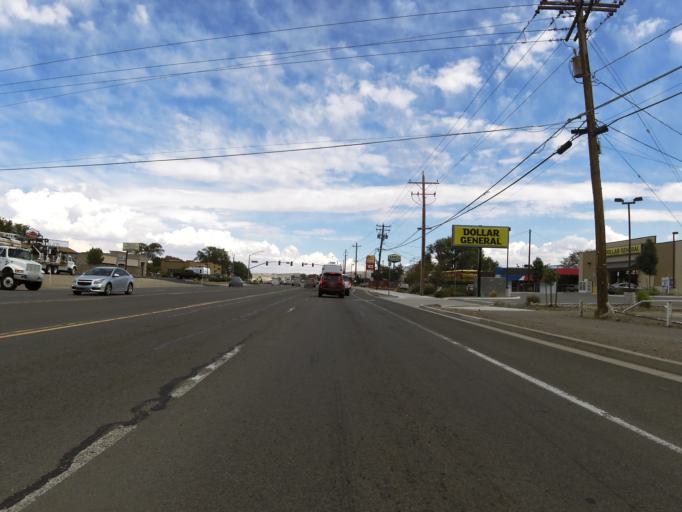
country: US
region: Nevada
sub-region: Carson City
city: Carson City
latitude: 39.1761
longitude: -119.7350
